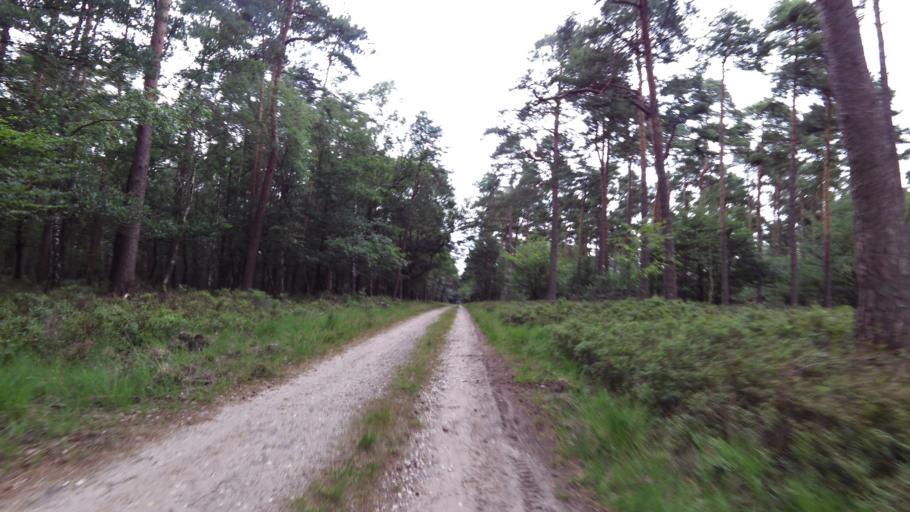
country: NL
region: Gelderland
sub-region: Gemeente Apeldoorn
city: Apeldoorn
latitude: 52.2068
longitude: 5.8917
